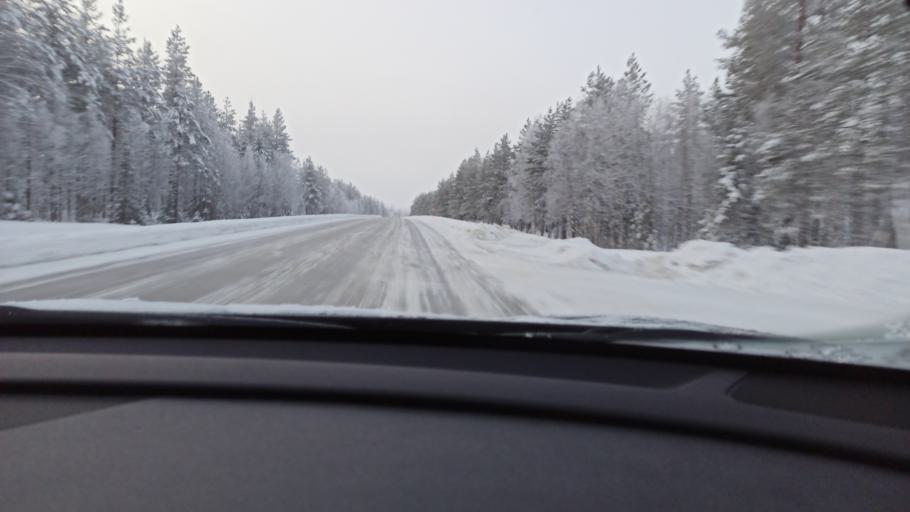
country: FI
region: Lapland
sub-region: Pohjois-Lappi
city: Sodankylae
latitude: 66.9804
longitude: 26.3258
